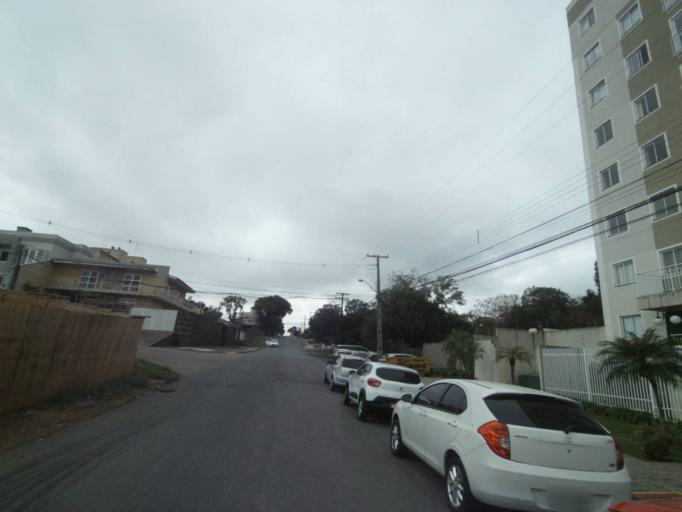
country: BR
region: Parana
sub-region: Curitiba
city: Curitiba
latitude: -25.5044
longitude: -49.2992
